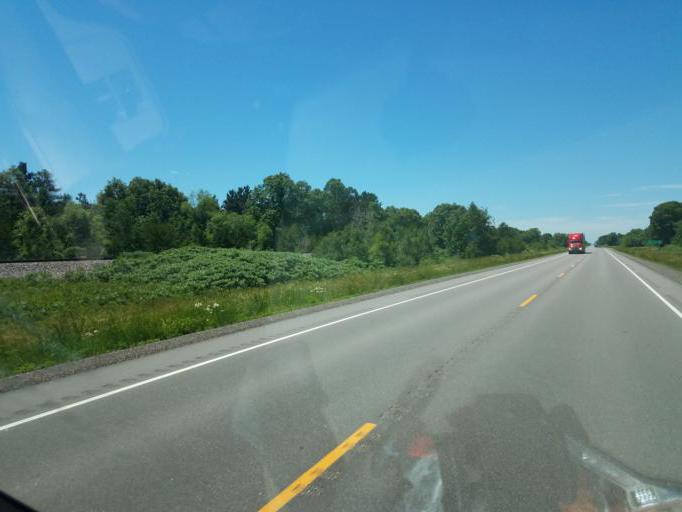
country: US
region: Wisconsin
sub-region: Juneau County
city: New Lisbon
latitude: 44.0248
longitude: -90.1291
